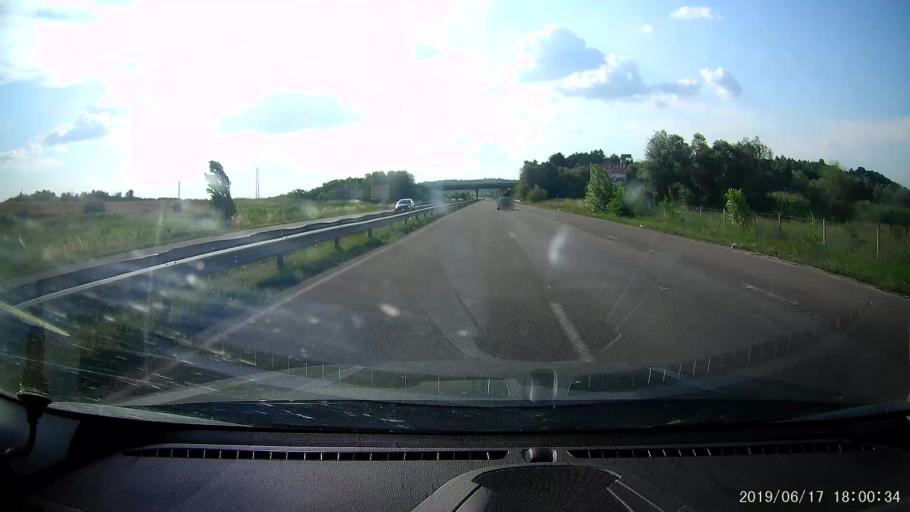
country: BG
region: Khaskovo
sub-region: Obshtina Svilengrad
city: Svilengrad
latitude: 41.7382
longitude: 26.2763
